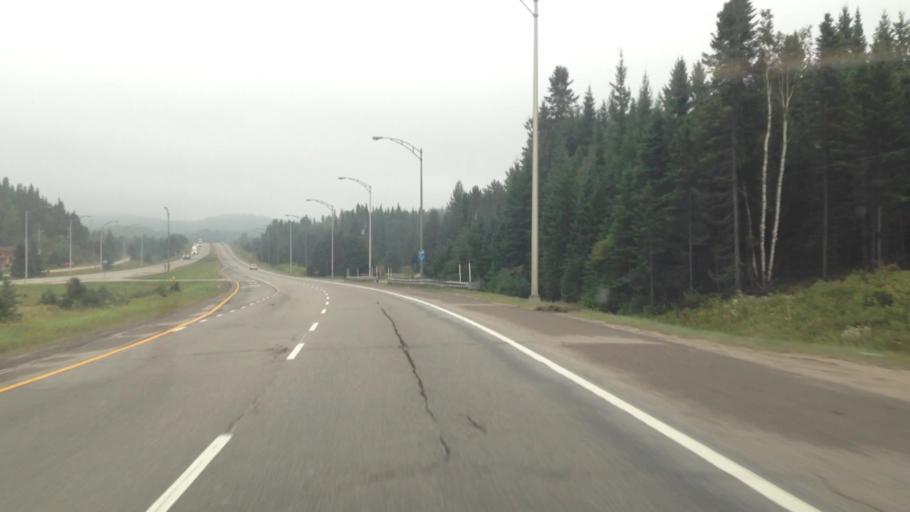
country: CA
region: Quebec
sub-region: Laurentides
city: Sainte-Agathe-des-Monts
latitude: 46.0989
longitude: -74.3729
